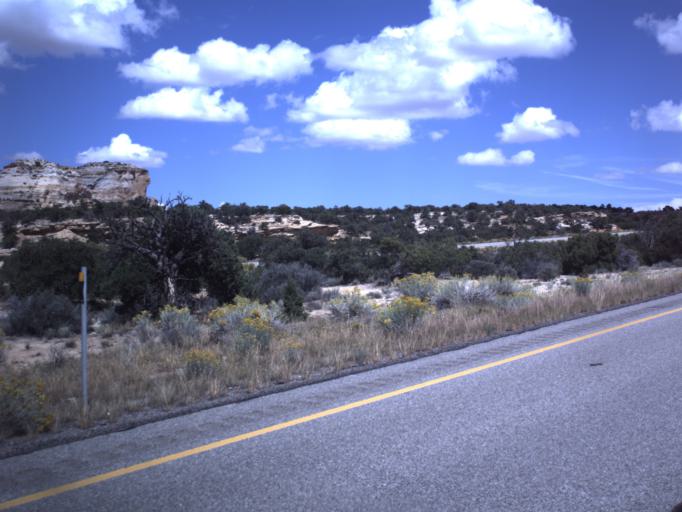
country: US
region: Utah
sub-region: Emery County
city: Ferron
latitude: 38.8627
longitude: -110.8576
